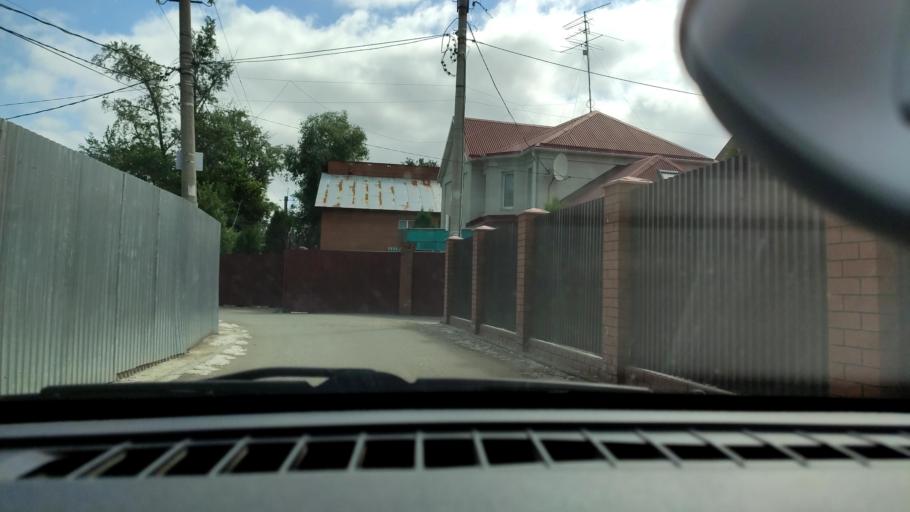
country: RU
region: Samara
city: Novokuybyshevsk
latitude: 53.1513
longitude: 49.9775
